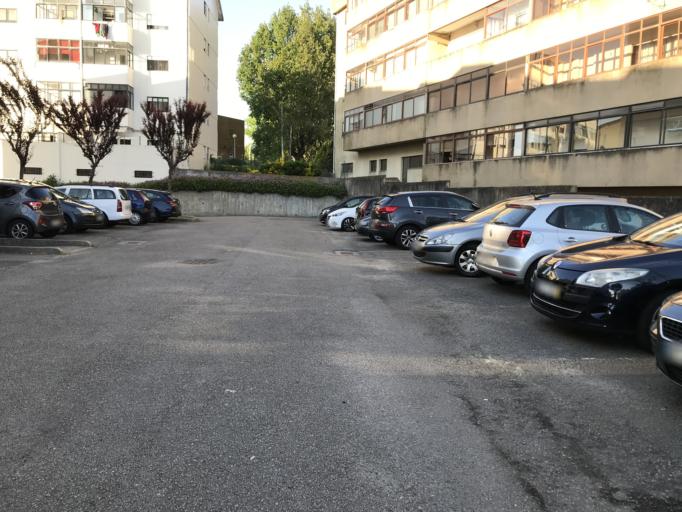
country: PT
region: Porto
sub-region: Matosinhos
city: Matosinhos
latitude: 41.1801
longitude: -8.6734
